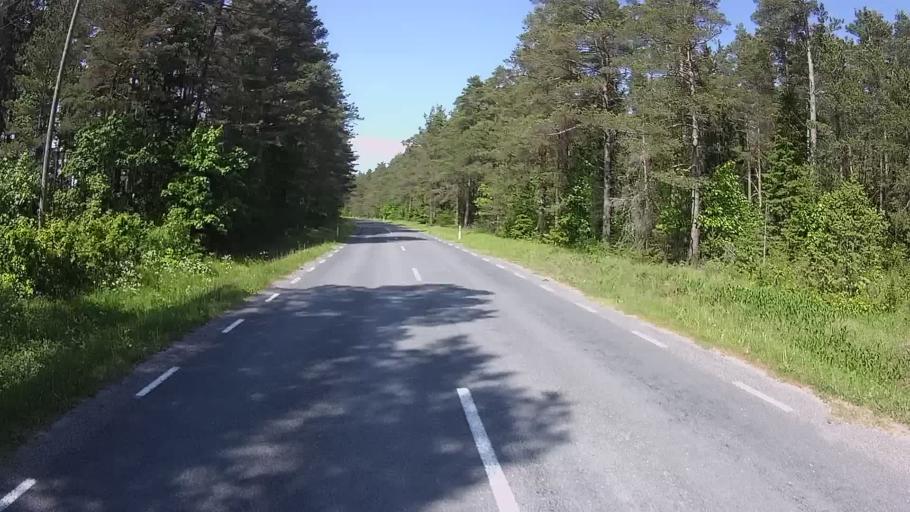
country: EE
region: Saare
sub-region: Kuressaare linn
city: Kuressaare
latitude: 58.4964
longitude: 22.4277
